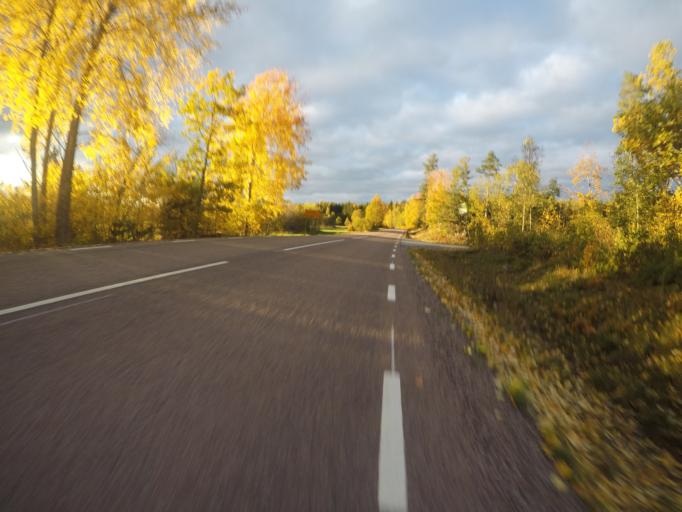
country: SE
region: Vaestmanland
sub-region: Arboga Kommun
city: Tyringe
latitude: 59.3118
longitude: 15.9869
